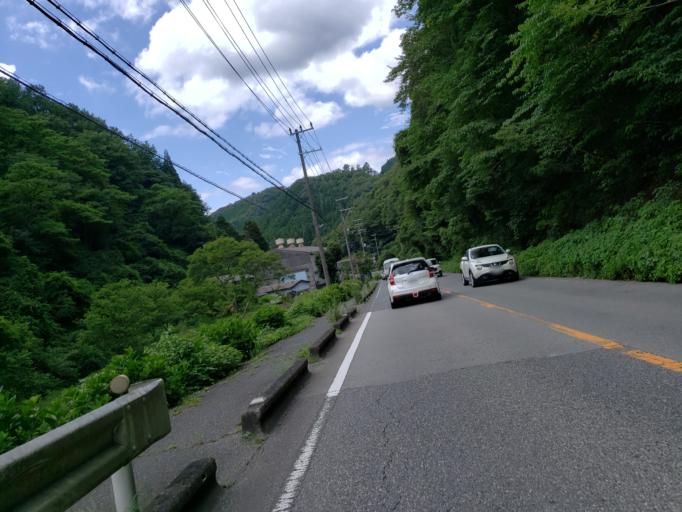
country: JP
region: Hyogo
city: Yamazakicho-nakabirose
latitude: 34.9844
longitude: 134.6118
